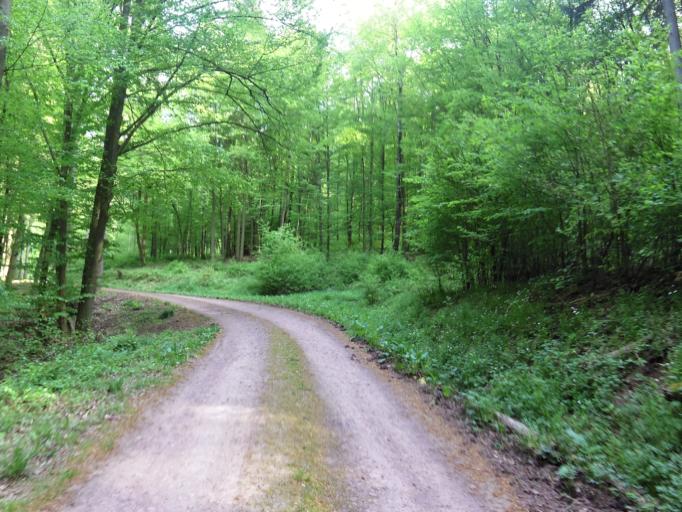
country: DE
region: Thuringia
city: Eisenach
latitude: 50.9621
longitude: 10.2984
